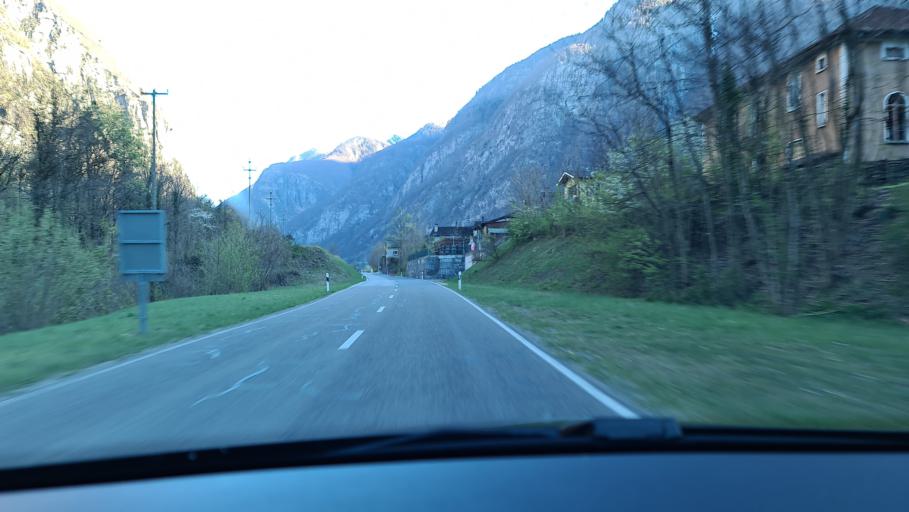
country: CH
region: Ticino
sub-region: Vallemaggia District
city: Cevio
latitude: 46.3160
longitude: 8.6029
